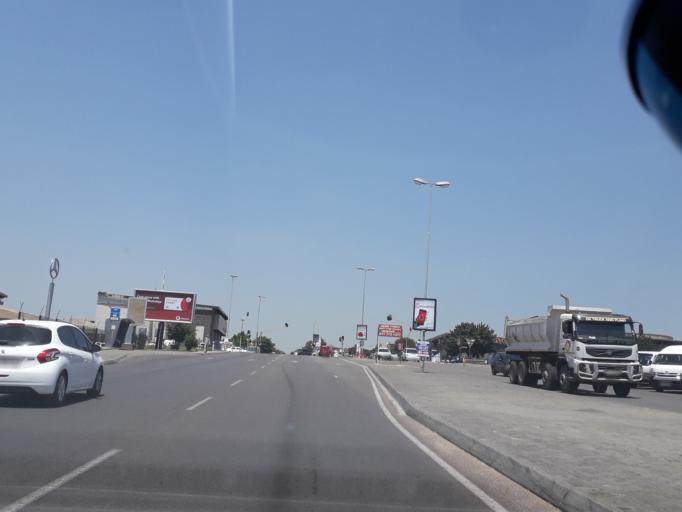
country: ZA
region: Gauteng
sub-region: City of Johannesburg Metropolitan Municipality
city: Midrand
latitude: -25.9772
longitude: 28.1188
